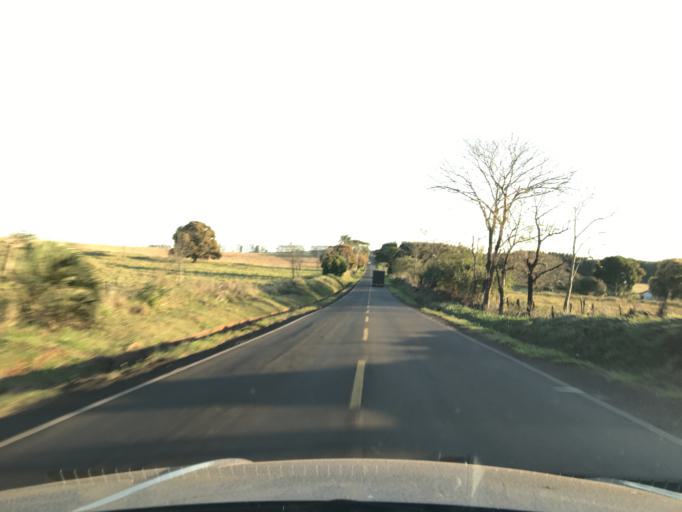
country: PY
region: Canindeyu
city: Salto del Guaira
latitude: -24.0925
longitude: -54.0955
